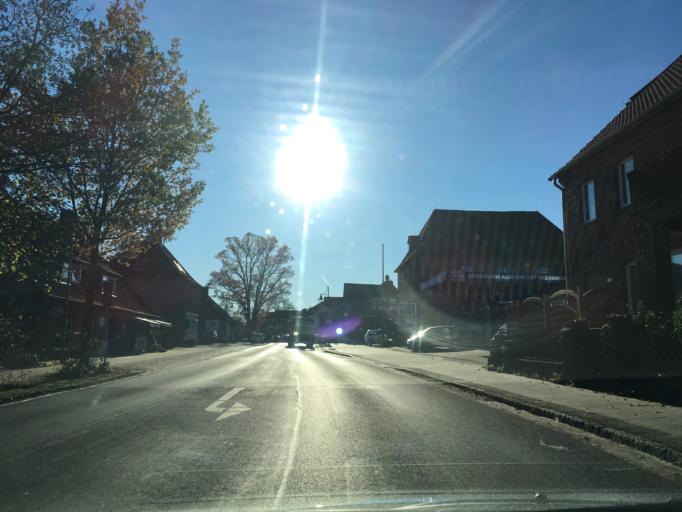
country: DE
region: Lower Saxony
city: Amelinghausen
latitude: 53.1288
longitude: 10.2161
